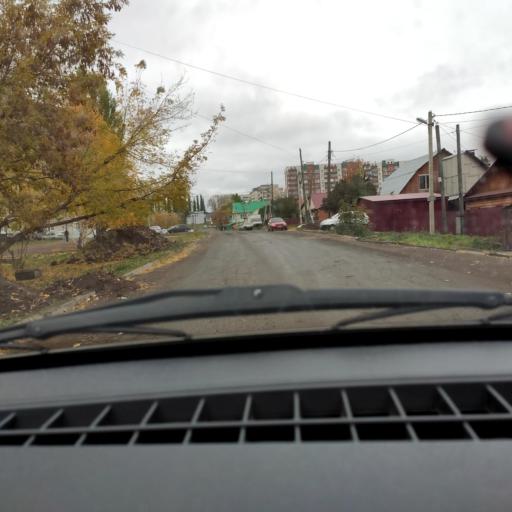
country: RU
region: Bashkortostan
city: Ufa
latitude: 54.8216
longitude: 56.1247
